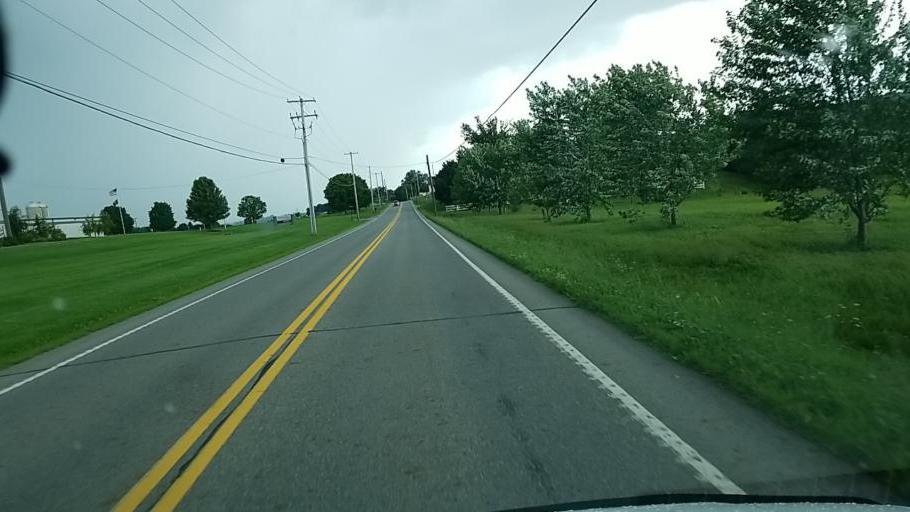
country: US
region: Pennsylvania
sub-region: Dauphin County
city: Elizabethville
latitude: 40.5824
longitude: -76.8701
